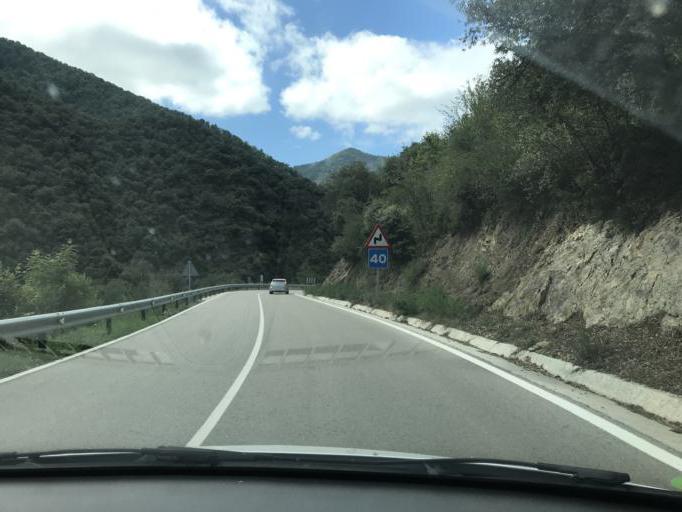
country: ES
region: Cantabria
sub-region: Provincia de Cantabria
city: Cabezon de Liebana
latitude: 43.0782
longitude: -4.5470
